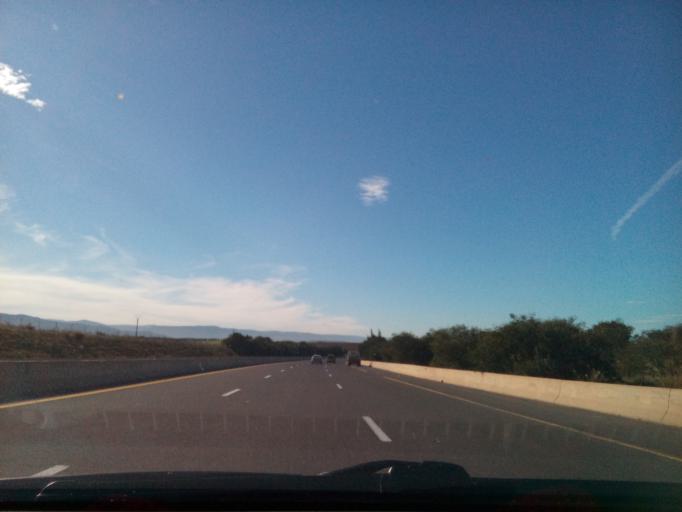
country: DZ
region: Tlemcen
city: Bensekrane
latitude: 34.9964
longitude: -1.1959
